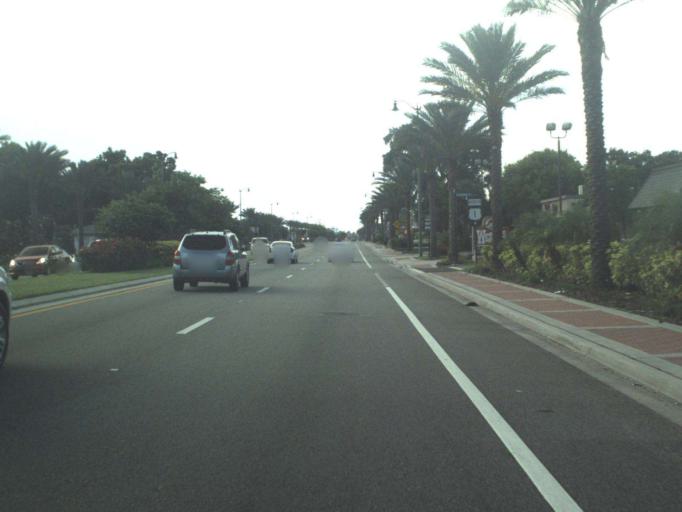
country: US
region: Florida
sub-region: Volusia County
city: South Daytona
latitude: 29.1745
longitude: -81.0033
